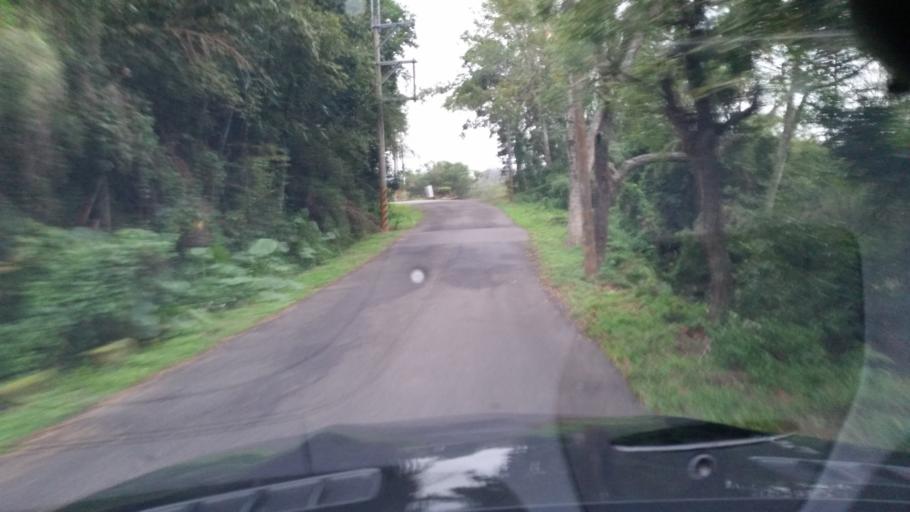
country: TW
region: Taiwan
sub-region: Miaoli
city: Miaoli
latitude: 24.5856
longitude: 120.8981
